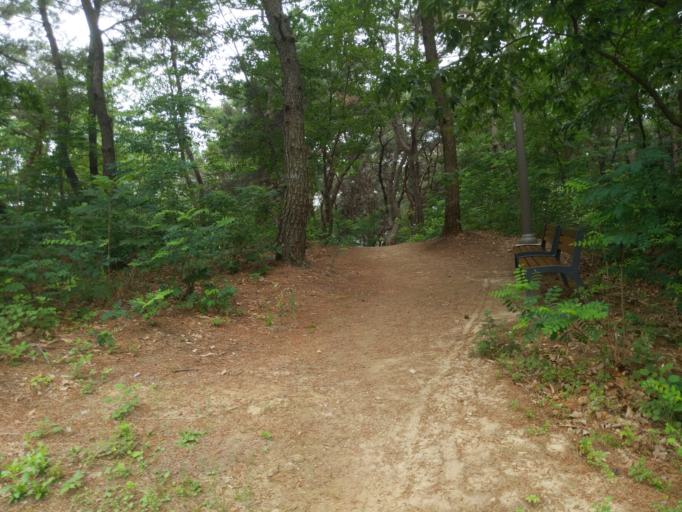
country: KR
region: Daegu
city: Hwawon
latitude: 35.8023
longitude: 128.5334
